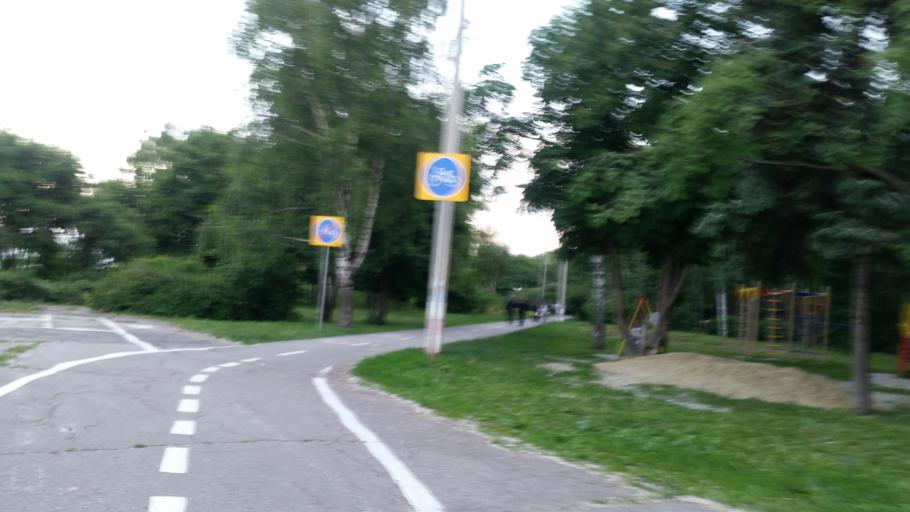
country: RU
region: Ulyanovsk
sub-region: Ulyanovskiy Rayon
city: Ulyanovsk
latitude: 54.3303
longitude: 48.4068
